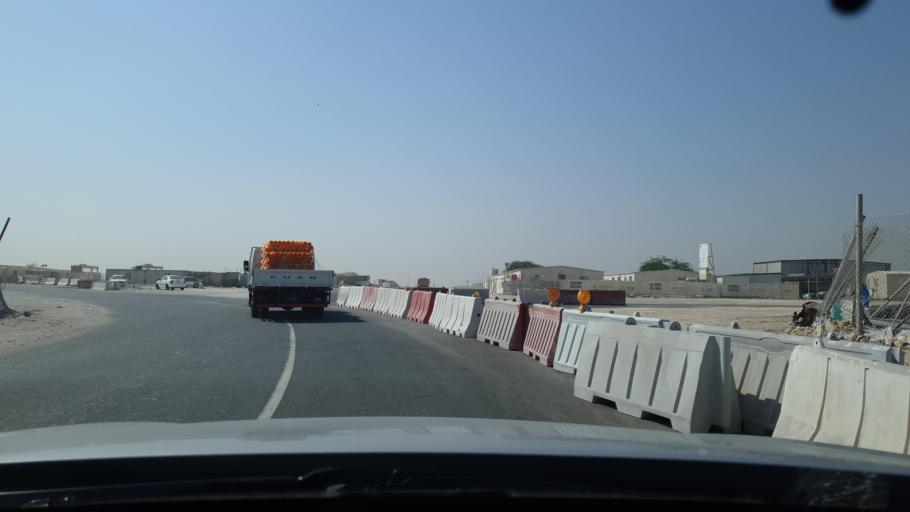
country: QA
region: Baladiyat ad Dawhah
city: Doha
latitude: 25.2297
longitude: 51.5218
